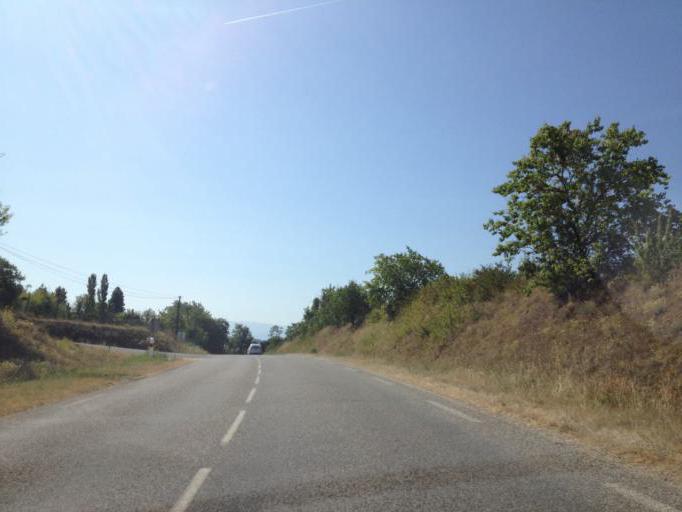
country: FR
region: Rhone-Alpes
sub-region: Departement de la Drome
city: Clerieux
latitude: 45.1284
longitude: 4.9553
